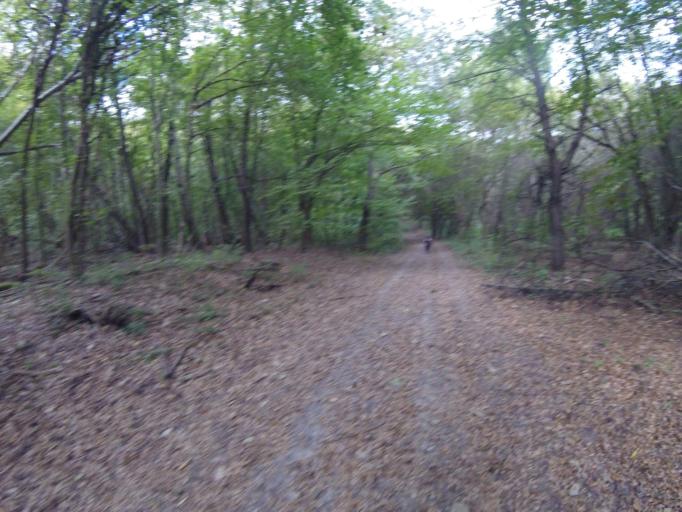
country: HU
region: Pest
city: Nagymaros
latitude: 47.8326
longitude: 18.9344
